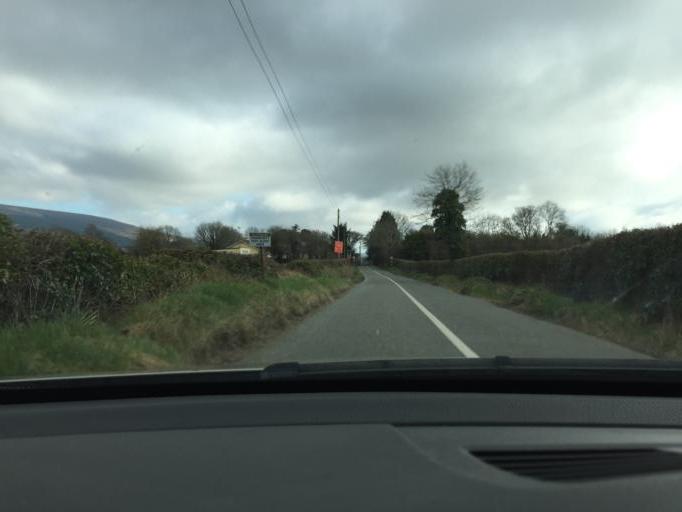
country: IE
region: Leinster
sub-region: Wicklow
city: Valleymount
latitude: 53.1099
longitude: -6.5270
